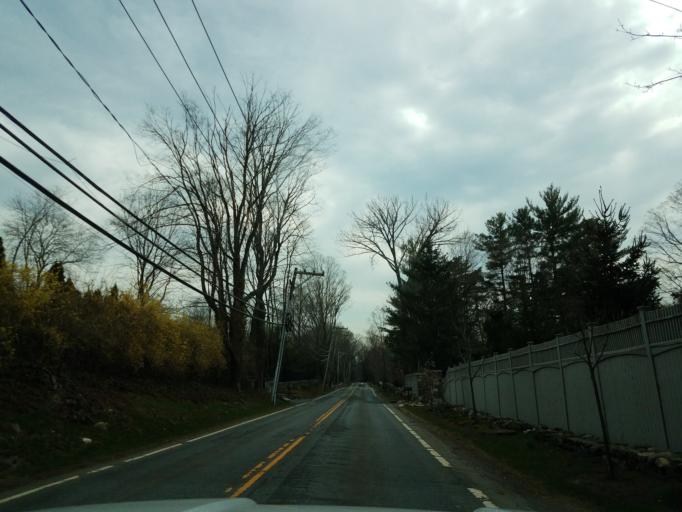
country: US
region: Connecticut
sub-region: Fairfield County
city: Glenville
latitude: 41.0588
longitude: -73.6392
